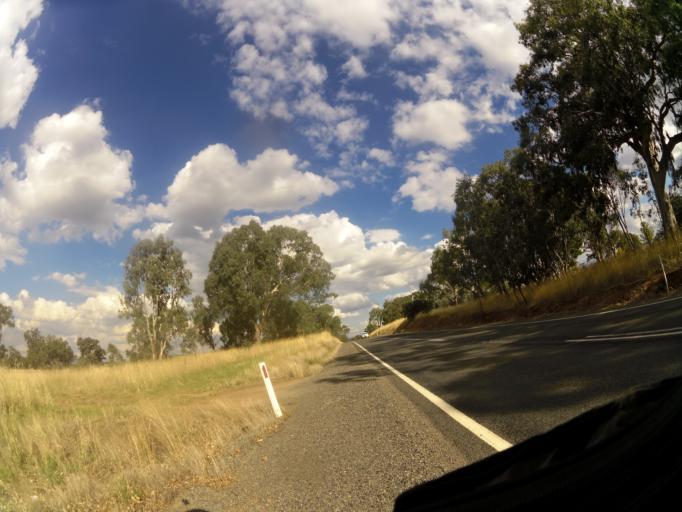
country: AU
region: Victoria
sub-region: Mansfield
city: Mansfield
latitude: -37.0148
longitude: 146.0881
